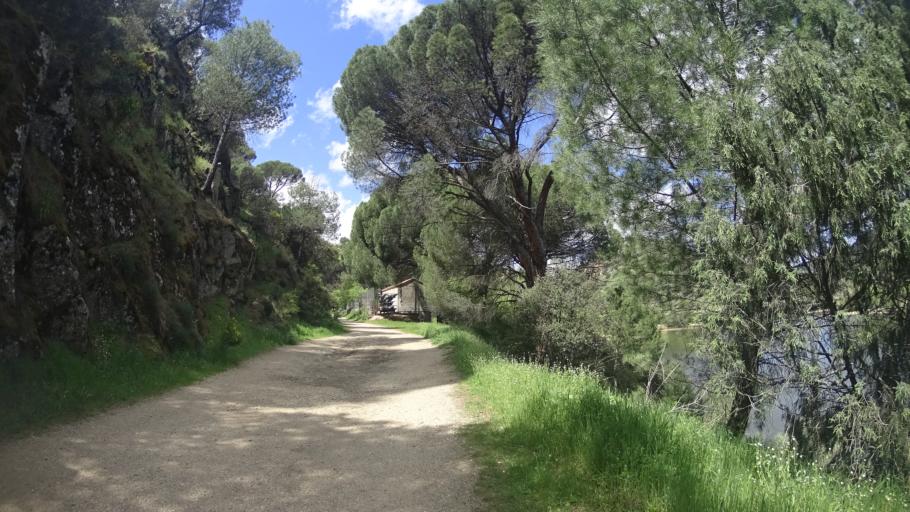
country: ES
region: Madrid
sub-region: Provincia de Madrid
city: Pelayos de la Presa
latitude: 40.3660
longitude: -4.3023
